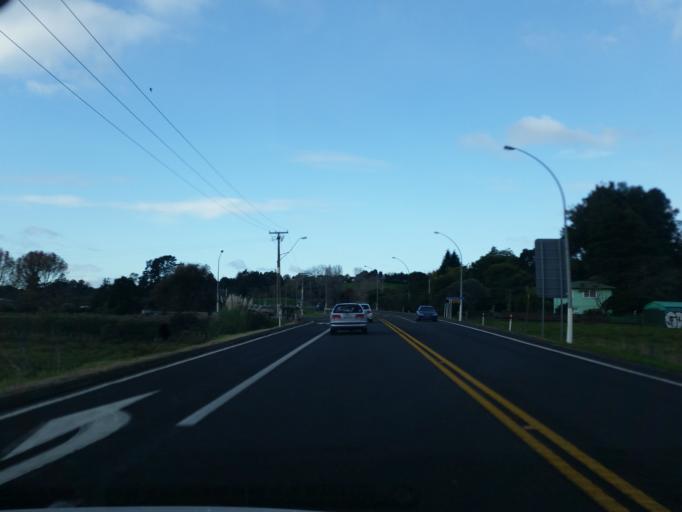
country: NZ
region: Bay of Plenty
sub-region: Tauranga City
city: Tauranga
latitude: -37.7001
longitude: 176.0912
